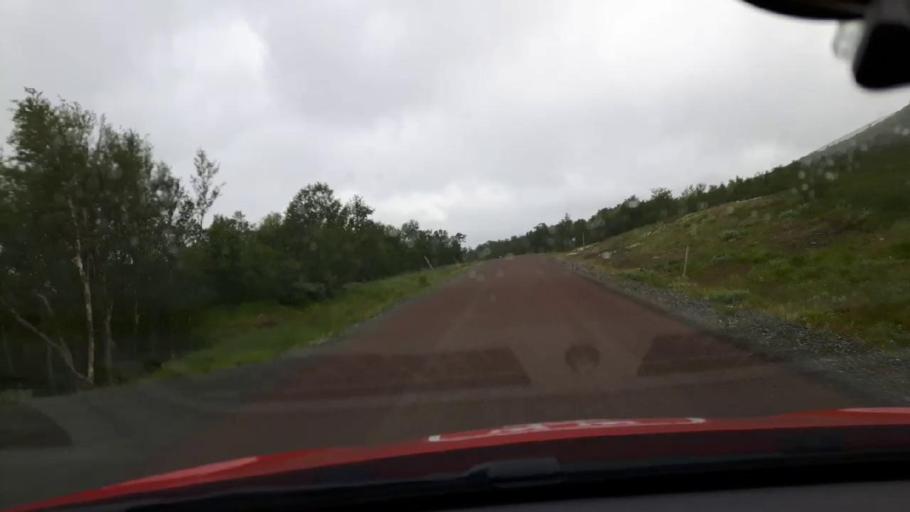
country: NO
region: Nord-Trondelag
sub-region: Meraker
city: Meraker
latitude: 63.1890
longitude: 12.3829
